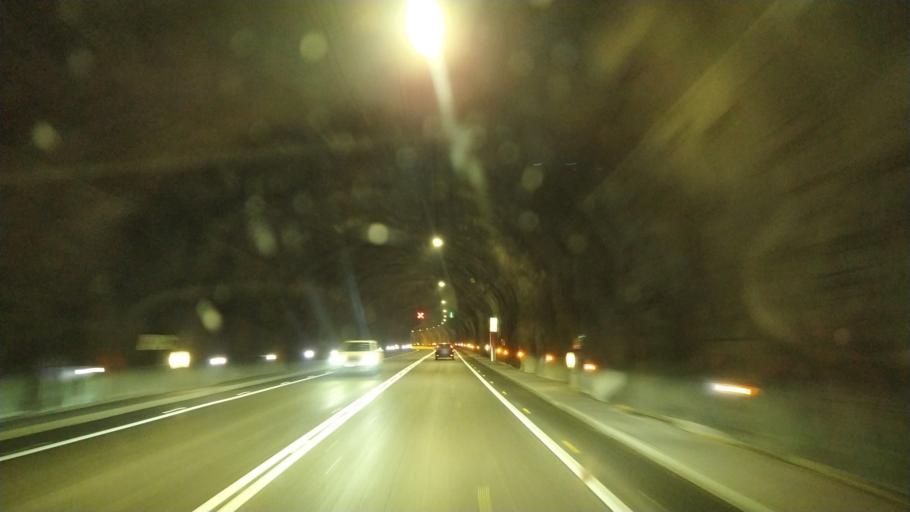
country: ES
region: Catalonia
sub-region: Provincia de Lleida
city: Coll de Nargo
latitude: 42.2532
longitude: 1.3495
